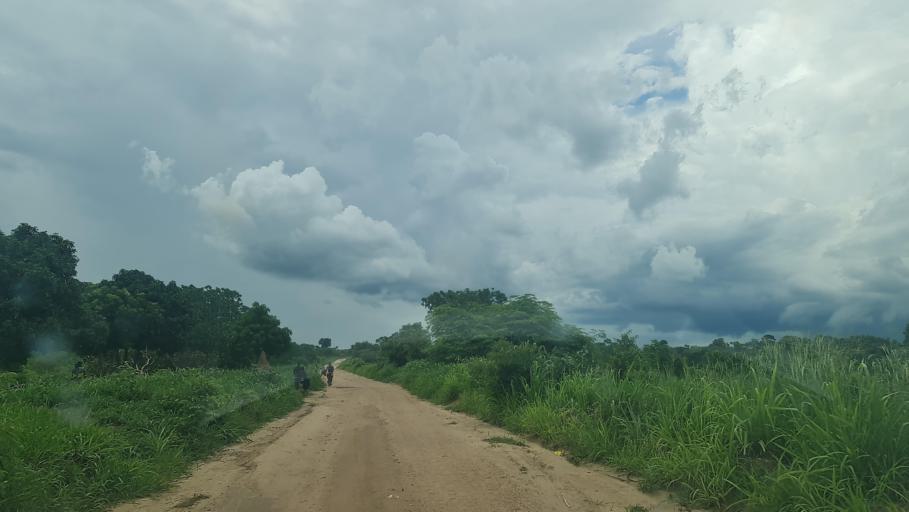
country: MW
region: Southern Region
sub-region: Nsanje District
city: Nsanje
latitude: -17.5684
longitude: 35.6488
